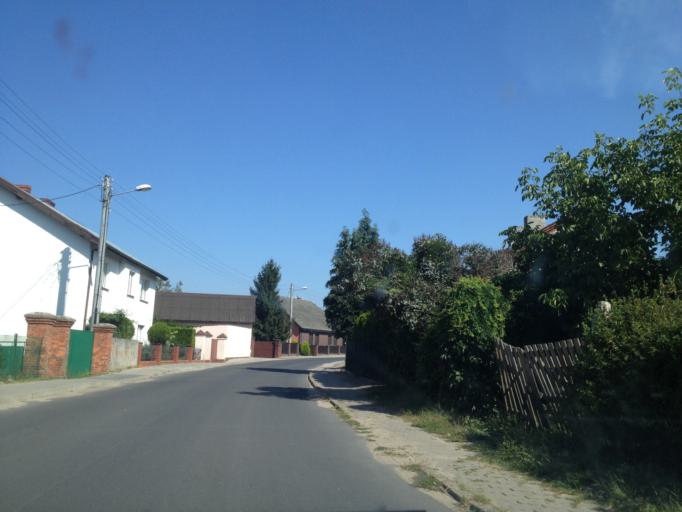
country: PL
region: Greater Poland Voivodeship
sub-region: Powiat sredzki
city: Zaniemysl
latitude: 52.1147
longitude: 17.1162
